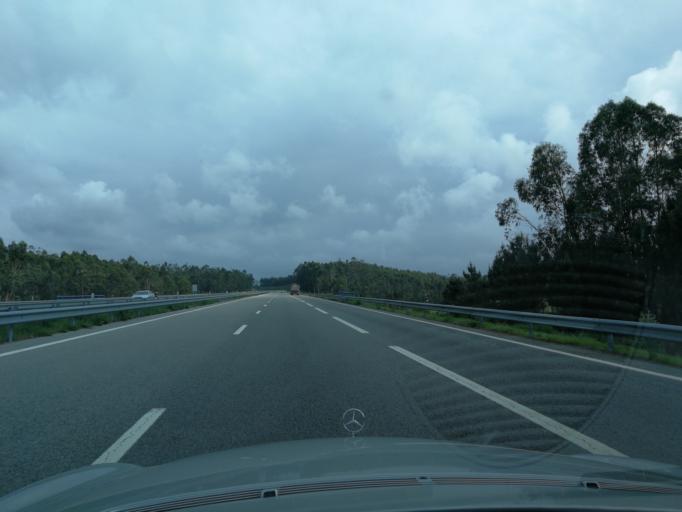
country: PT
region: Porto
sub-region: Vila do Conde
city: Arvore
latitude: 41.3868
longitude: -8.6691
